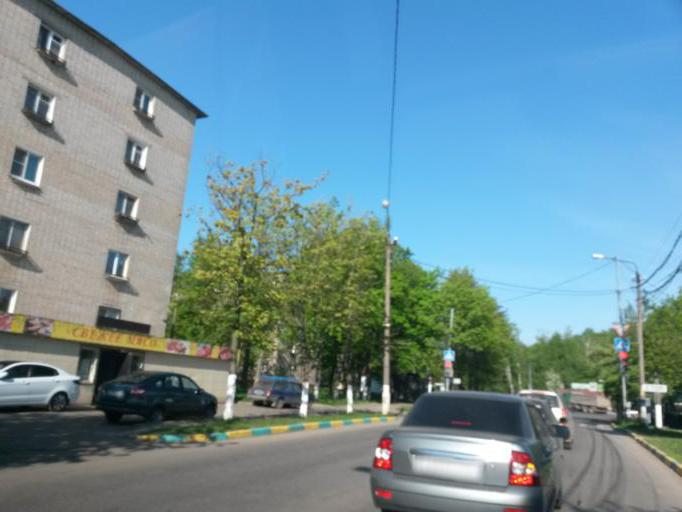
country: RU
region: Moskovskaya
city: Razvilka
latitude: 55.5923
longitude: 37.7546
